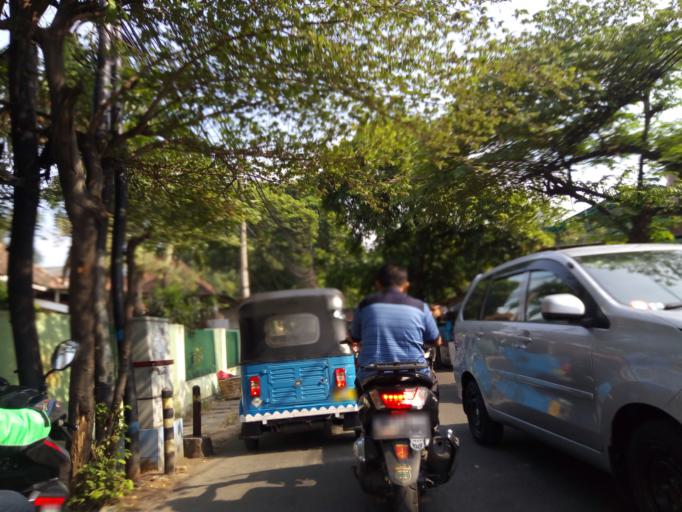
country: ID
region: Jakarta Raya
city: Jakarta
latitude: -6.2099
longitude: 106.8369
